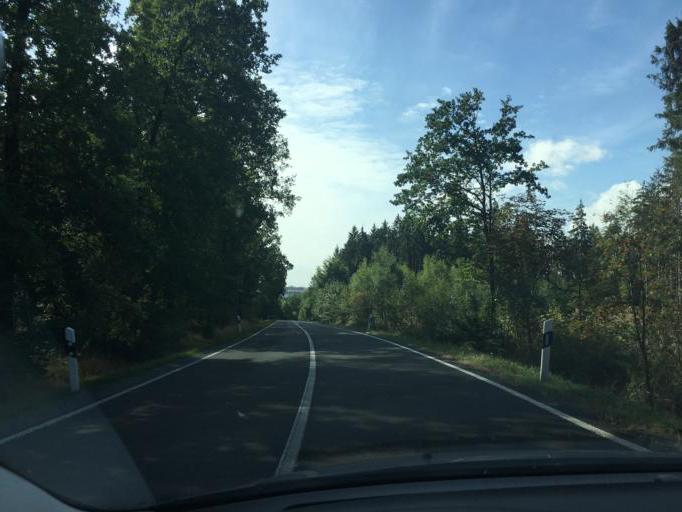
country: DE
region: Thuringia
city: Auma
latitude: 50.7161
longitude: 11.9046
